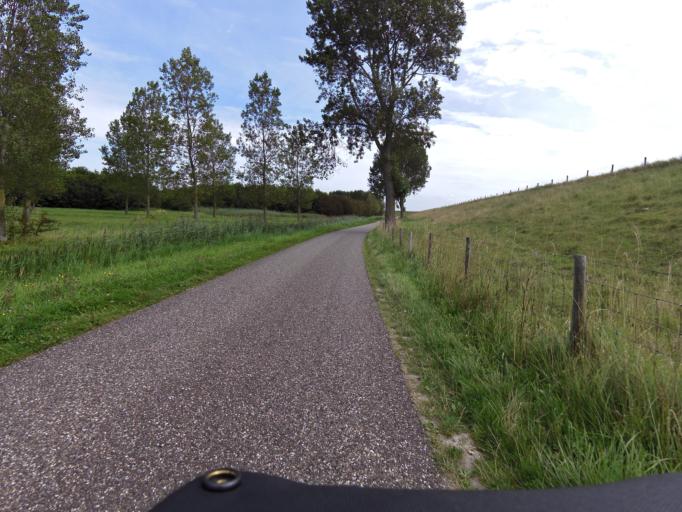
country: NL
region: South Holland
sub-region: Gemeente Goeree-Overflakkee
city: Middelharnis
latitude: 51.6861
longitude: 4.1671
